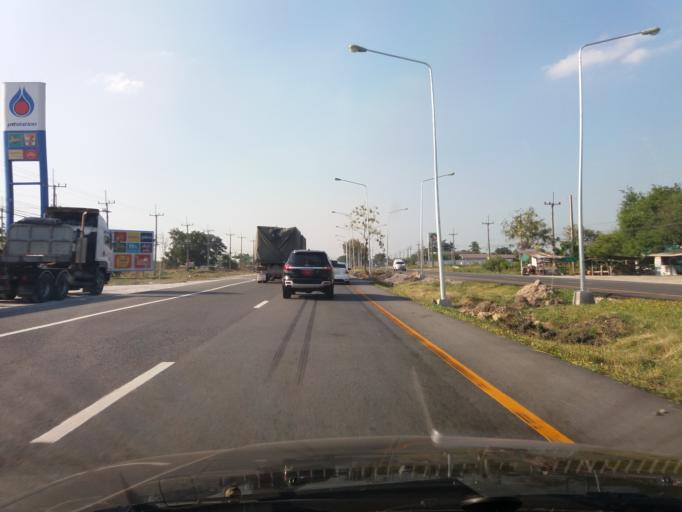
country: TH
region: Nakhon Sawan
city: Banphot Phisai
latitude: 15.8160
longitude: 99.9431
